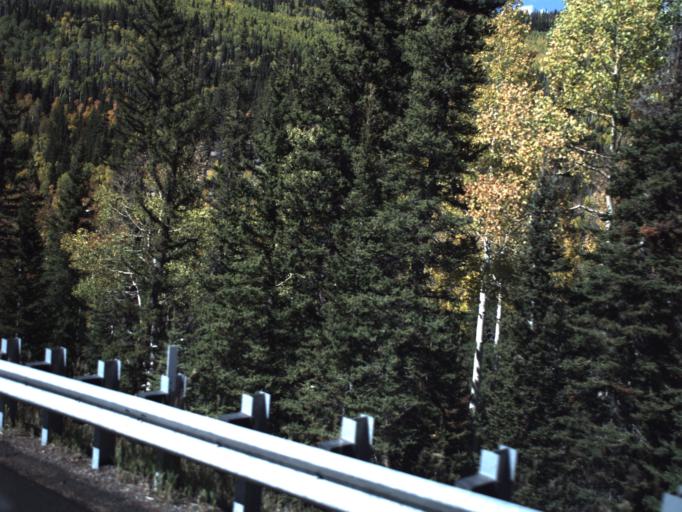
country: US
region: Utah
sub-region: Piute County
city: Junction
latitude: 38.3094
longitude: -112.4122
